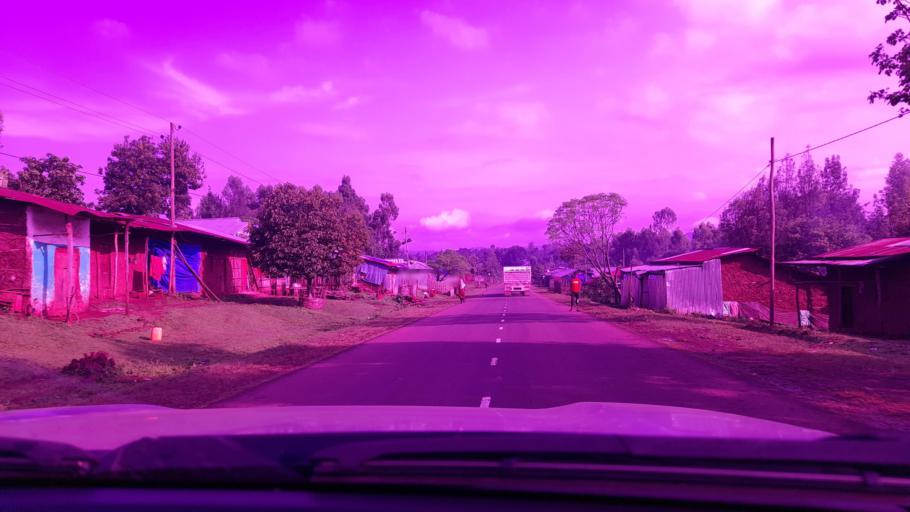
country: ET
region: Oromiya
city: Bedele
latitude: 8.1771
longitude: 36.4574
